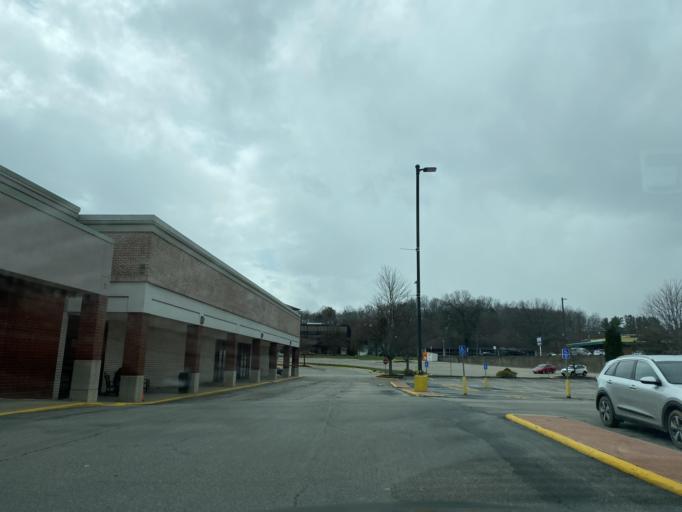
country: US
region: Ohio
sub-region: Summit County
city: Fairlawn
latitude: 41.1264
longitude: -81.6028
